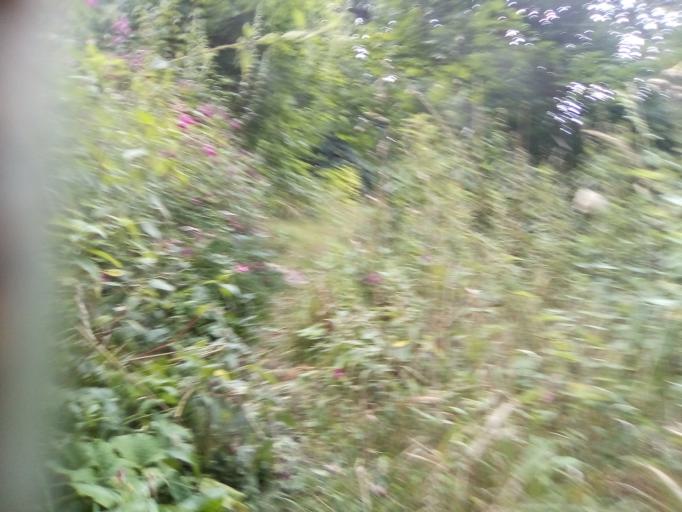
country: RU
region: Moskovskaya
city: Kokoshkino
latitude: 55.6160
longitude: 37.1656
